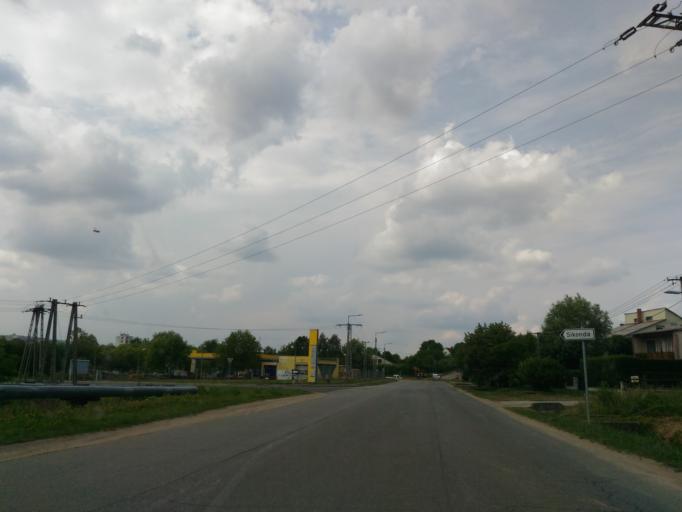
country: HU
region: Baranya
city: Komlo
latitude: 46.1866
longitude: 18.2420
